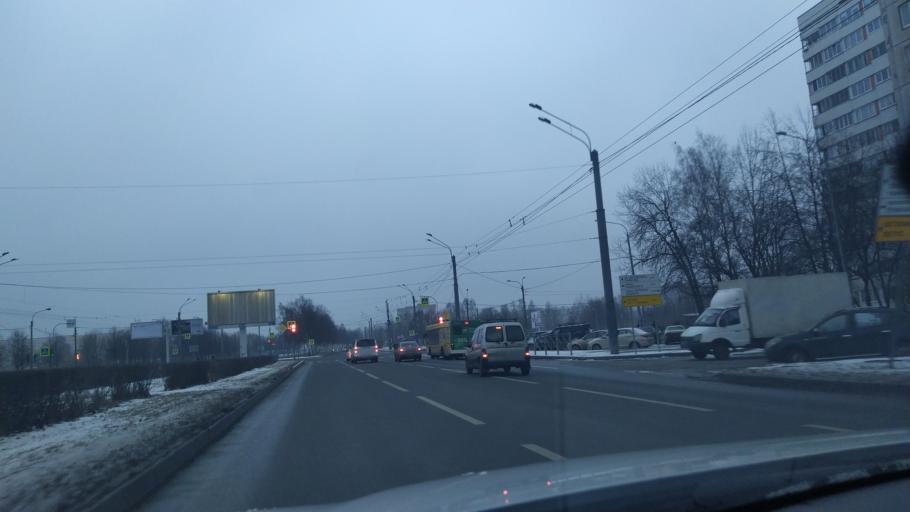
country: RU
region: St.-Petersburg
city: Grazhdanka
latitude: 60.0318
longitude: 30.3923
